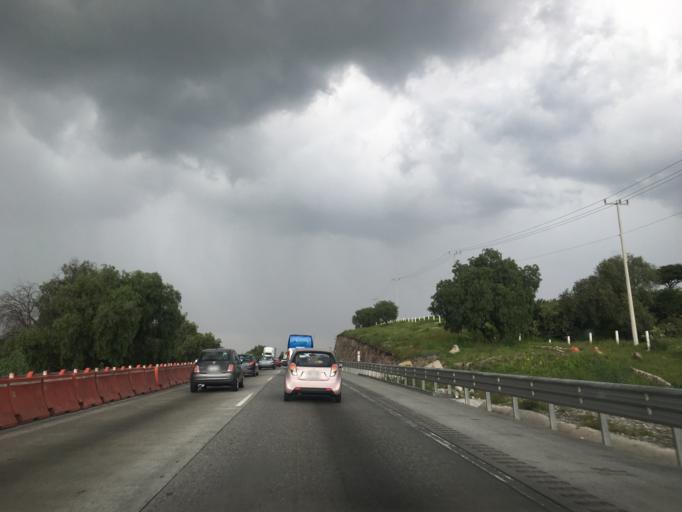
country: MX
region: Hidalgo
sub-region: Tepeji del Rio de Ocampo
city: Santiago Tlapanaloya
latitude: 19.8637
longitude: -99.3251
